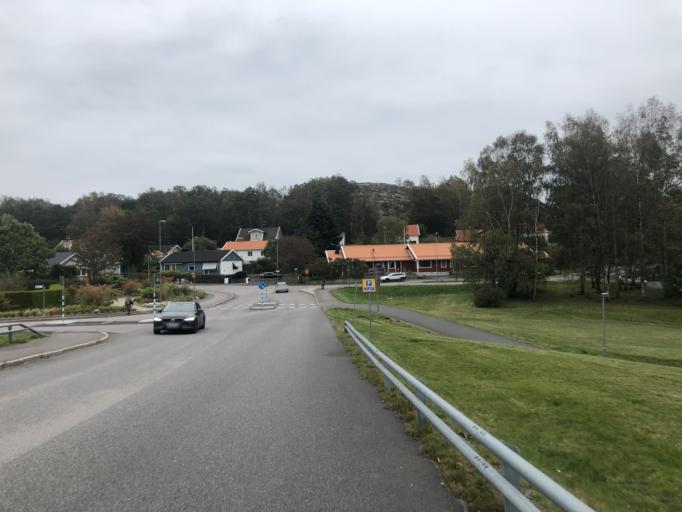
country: SE
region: Vaestra Goetaland
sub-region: Molndal
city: Moelndal
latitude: 57.6594
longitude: 12.0267
